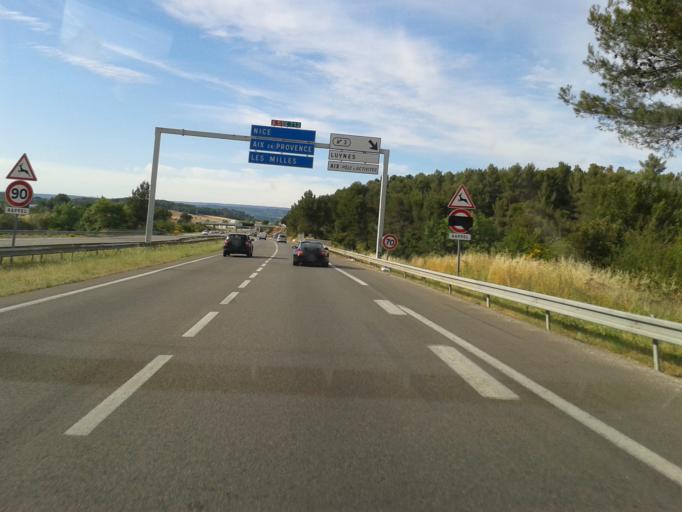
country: FR
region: Provence-Alpes-Cote d'Azur
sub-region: Departement des Bouches-du-Rhone
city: Bouc-Bel-Air
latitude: 43.4662
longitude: 5.4074
